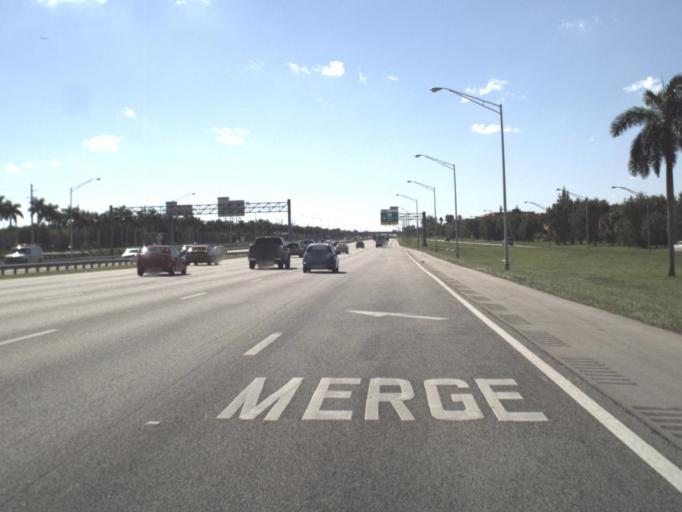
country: US
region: Florida
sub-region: Miami-Dade County
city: Tamiami
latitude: 25.7575
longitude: -80.3854
